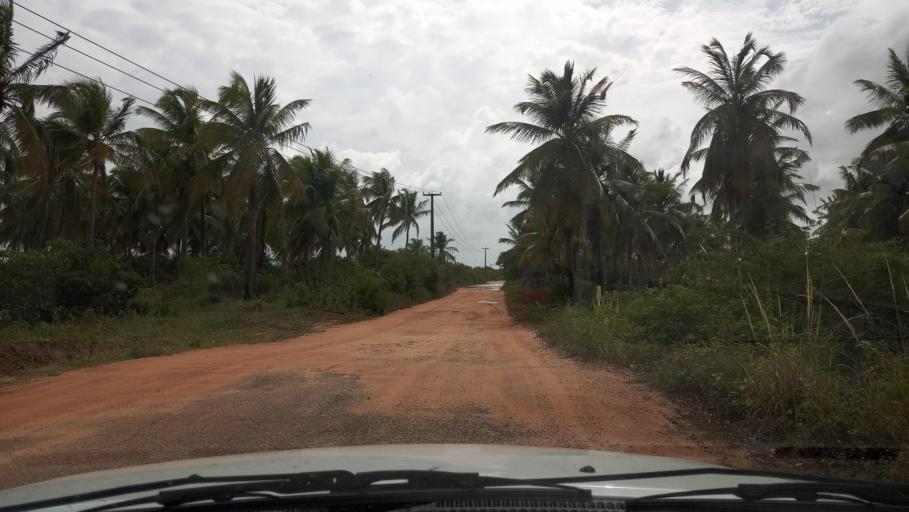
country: BR
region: Rio Grande do Norte
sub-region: Maxaranguape
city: Sao Miguel
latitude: -5.4832
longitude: -35.3238
